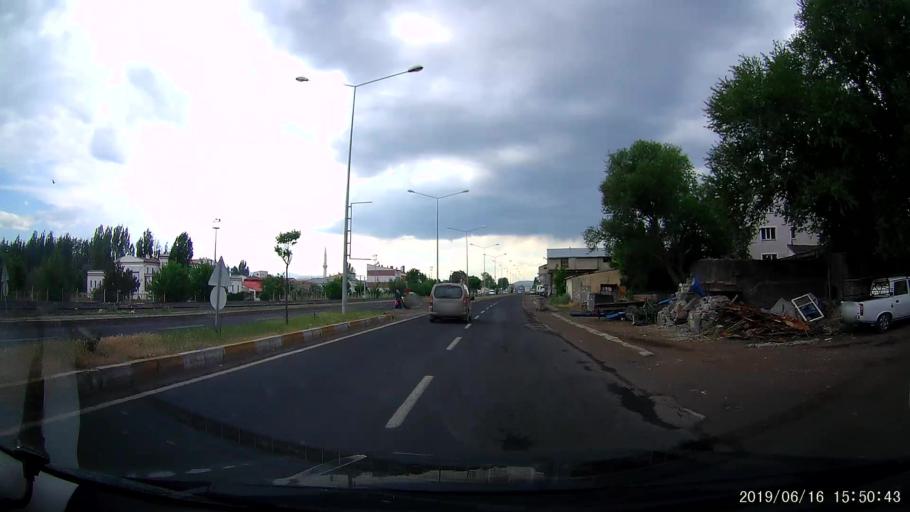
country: TR
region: Erzurum
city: Pasinler
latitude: 39.9771
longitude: 41.6793
